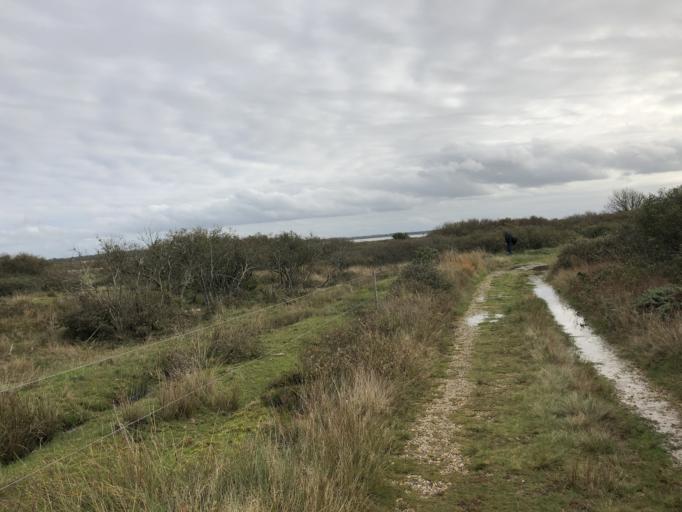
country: DK
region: South Denmark
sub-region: Varde Kommune
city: Oksbol
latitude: 55.7153
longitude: 8.2182
